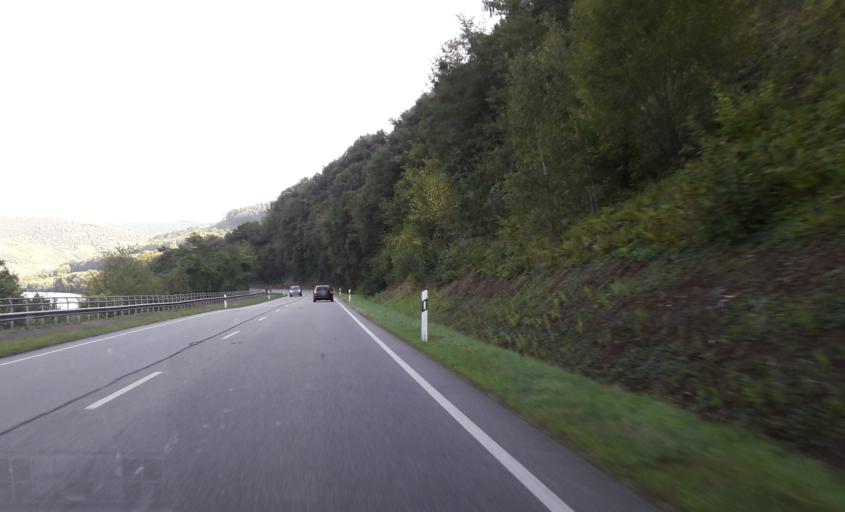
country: DE
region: Rheinland-Pfalz
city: Alf
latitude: 50.0453
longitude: 7.1370
